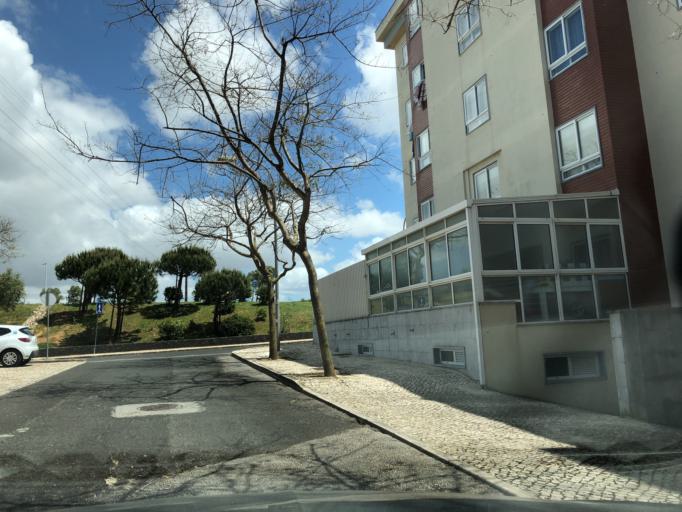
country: PT
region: Lisbon
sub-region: Cascais
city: Sao Domingos de Rana
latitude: 38.7123
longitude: -9.3257
